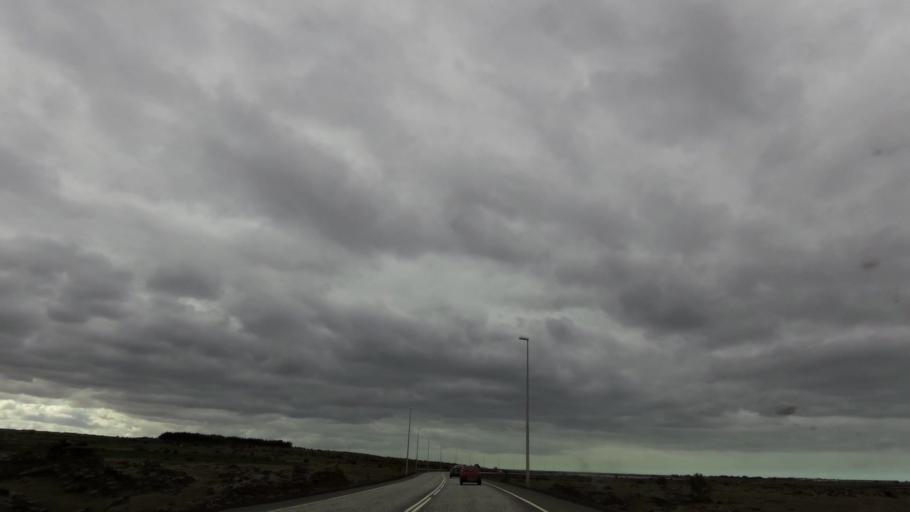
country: IS
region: Capital Region
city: Alftanes
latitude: 64.0910
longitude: -21.9745
